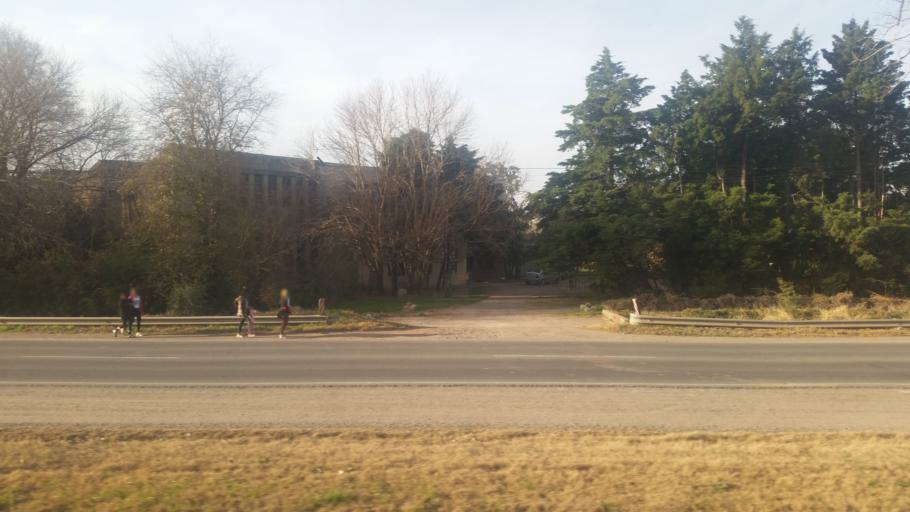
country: AR
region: Cordoba
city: Toledo
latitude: -31.4875
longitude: -64.0800
